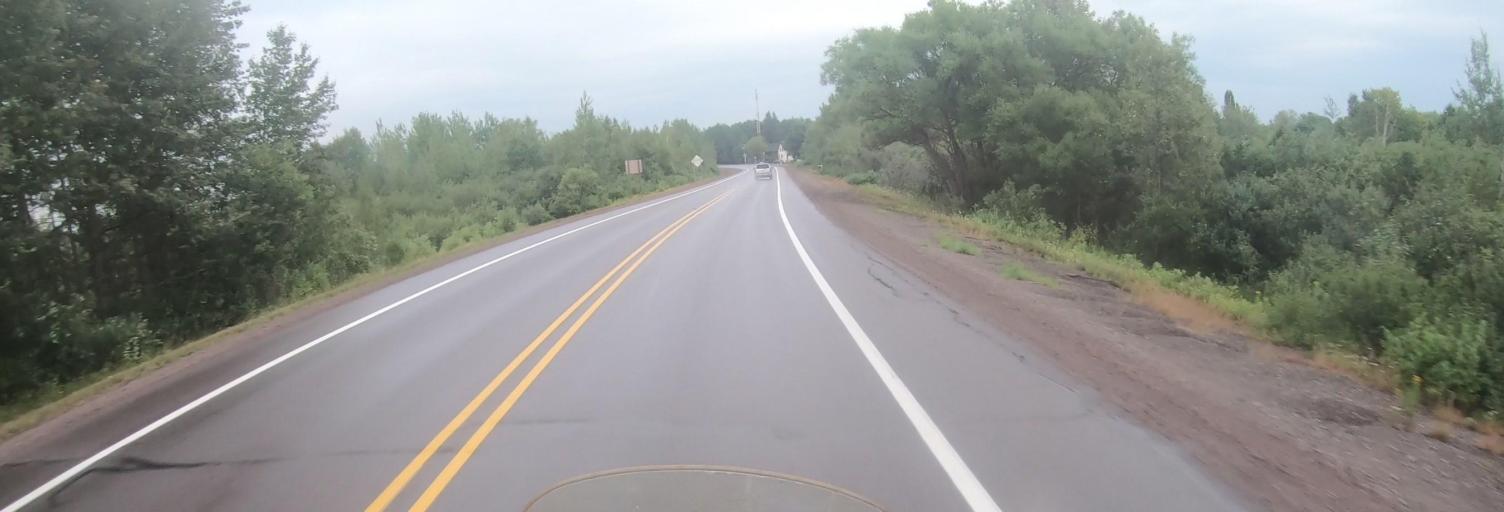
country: US
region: Michigan
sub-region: Houghton County
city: Laurium
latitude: 47.2519
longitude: -88.4376
